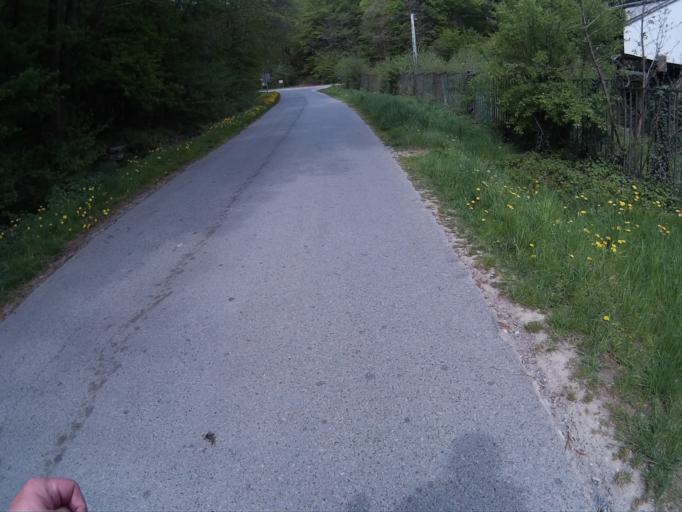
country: AT
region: Burgenland
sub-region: Politischer Bezirk Oberwart
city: Rechnitz
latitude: 47.3496
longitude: 16.4857
